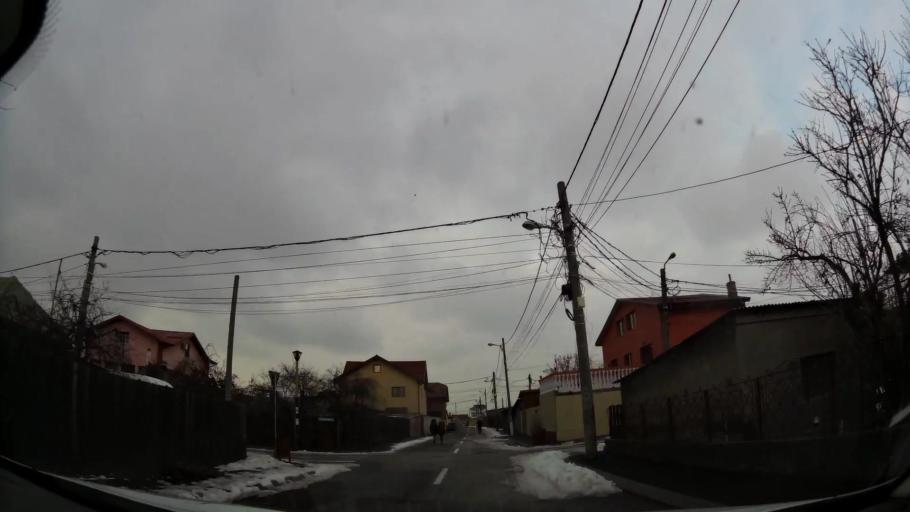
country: RO
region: Ilfov
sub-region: Voluntari City
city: Voluntari
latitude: 44.4834
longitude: 26.1866
